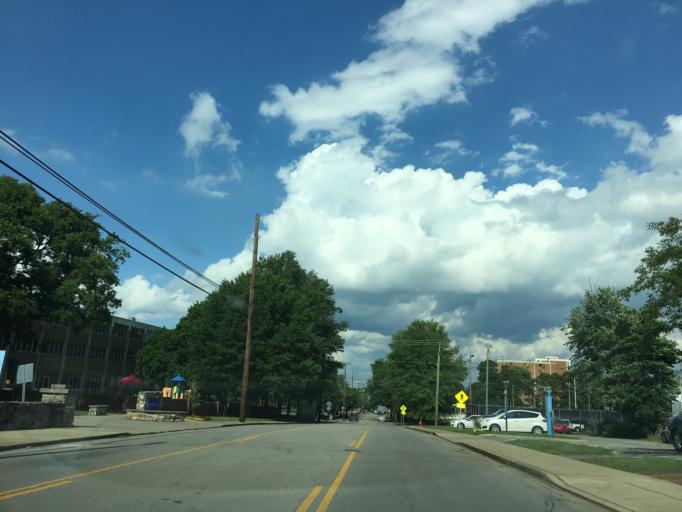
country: US
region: Tennessee
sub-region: Davidson County
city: Nashville
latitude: 36.1674
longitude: -86.8255
